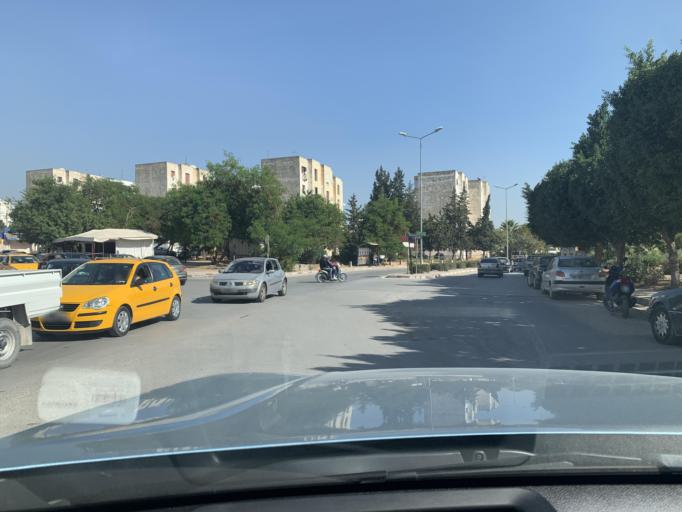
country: TN
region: Manouba
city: Manouba
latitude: 36.8271
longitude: 10.1212
